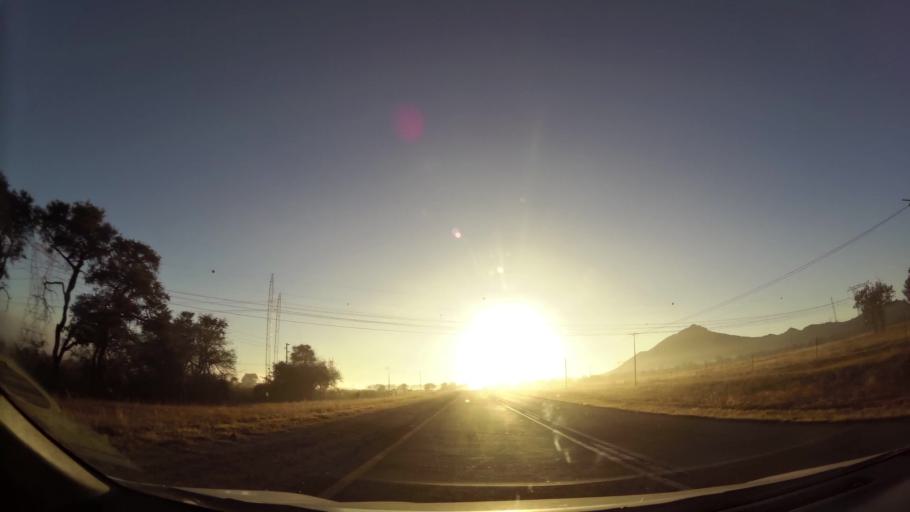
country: ZA
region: Limpopo
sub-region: Capricorn District Municipality
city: Polokwane
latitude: -24.0292
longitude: 29.2913
